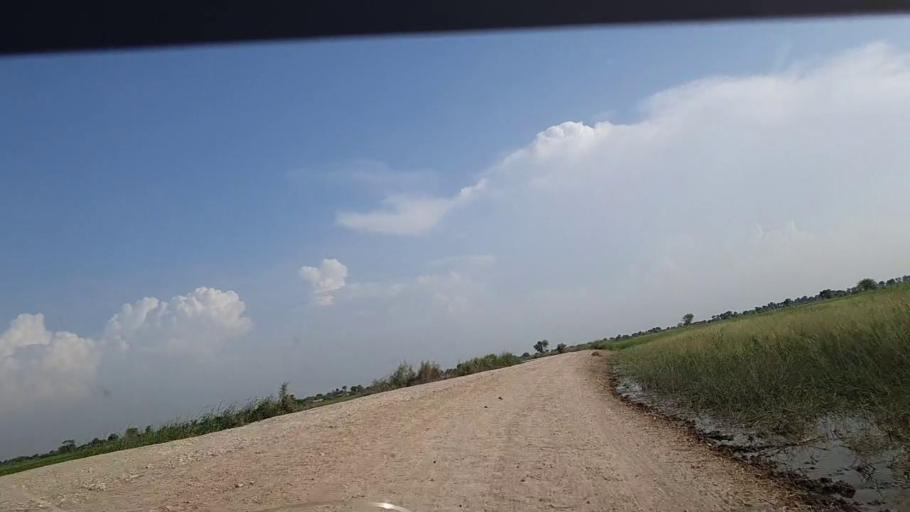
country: PK
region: Sindh
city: Khanpur
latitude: 27.8550
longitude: 69.3772
